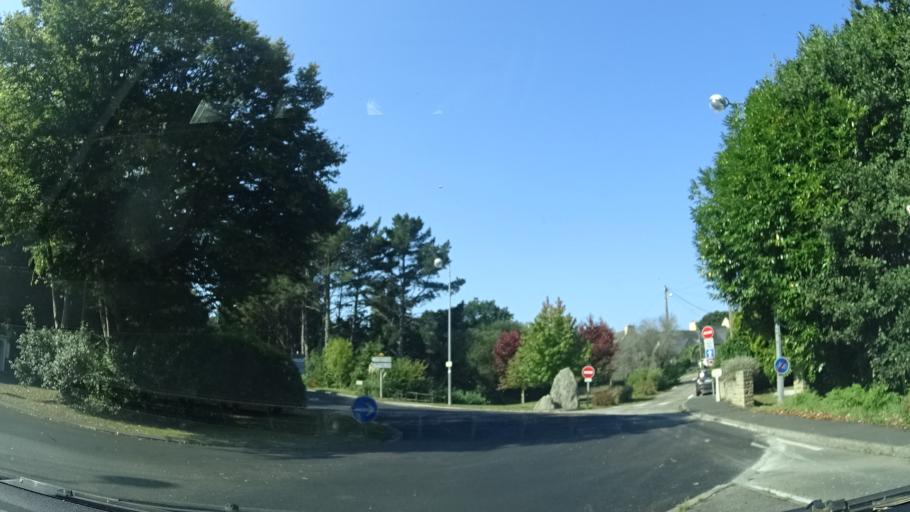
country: FR
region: Brittany
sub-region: Departement du Finistere
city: Douarnenez
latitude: 48.0865
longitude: -4.3409
